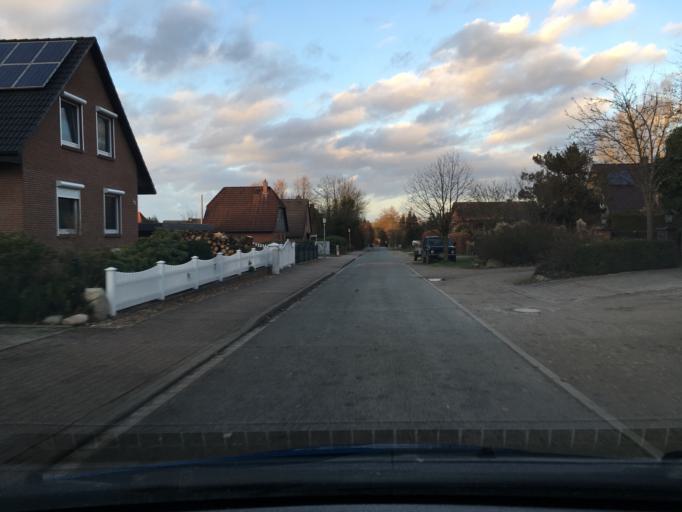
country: DE
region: Lower Saxony
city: Amelinghausen
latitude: 53.1351
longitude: 10.2191
